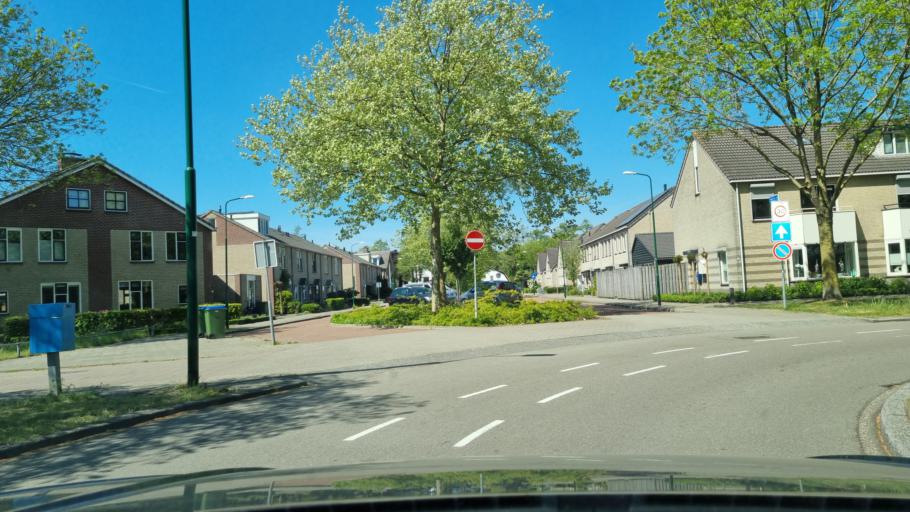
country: NL
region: Utrecht
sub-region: Gemeente Veenendaal
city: Veenendaal
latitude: 52.0356
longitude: 5.5306
